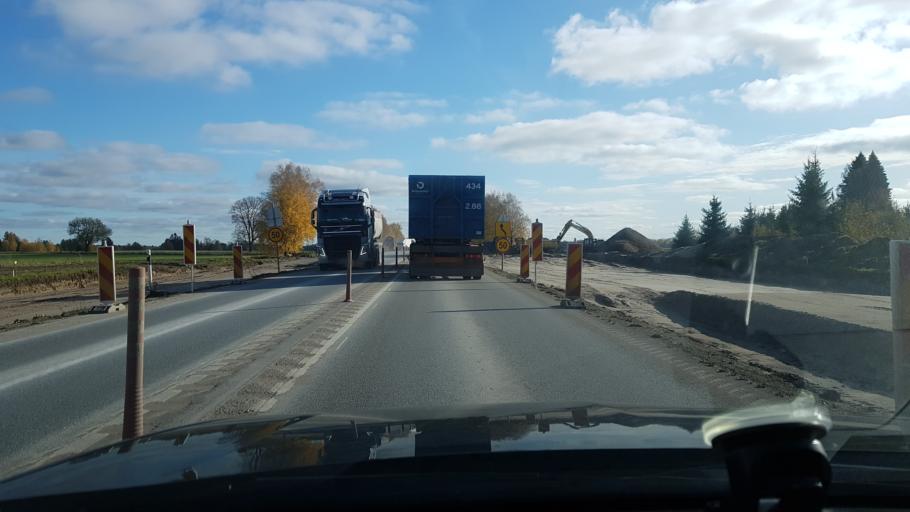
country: EE
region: Laeaene-Virumaa
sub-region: Haljala vald
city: Haljala
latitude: 59.4346
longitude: 26.1745
